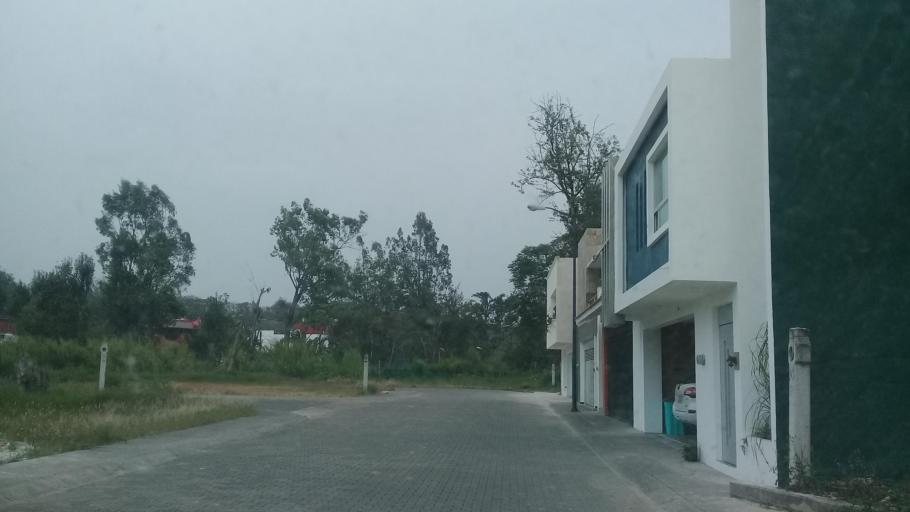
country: MX
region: Veracruz
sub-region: Xalapa
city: Xalapa de Enriquez
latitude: 19.5182
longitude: -96.9066
